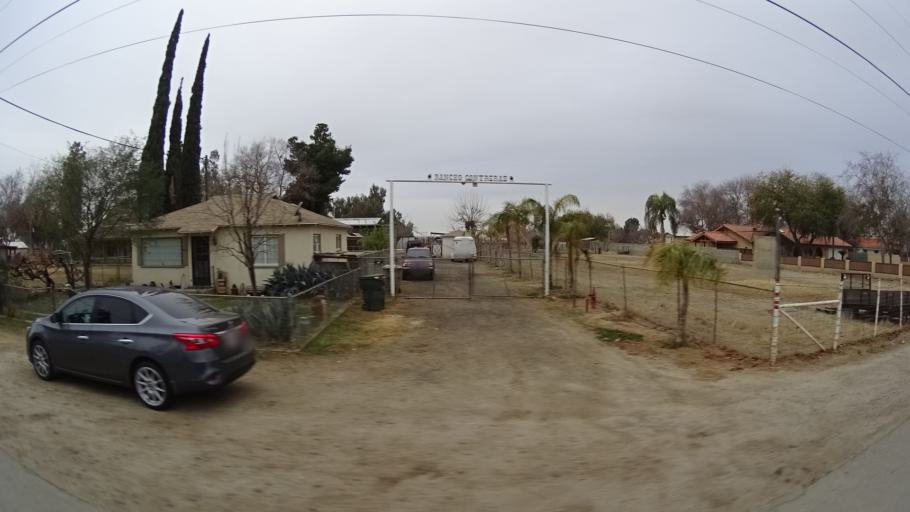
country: US
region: California
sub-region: Kern County
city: Lamont
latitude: 35.3277
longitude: -118.9321
